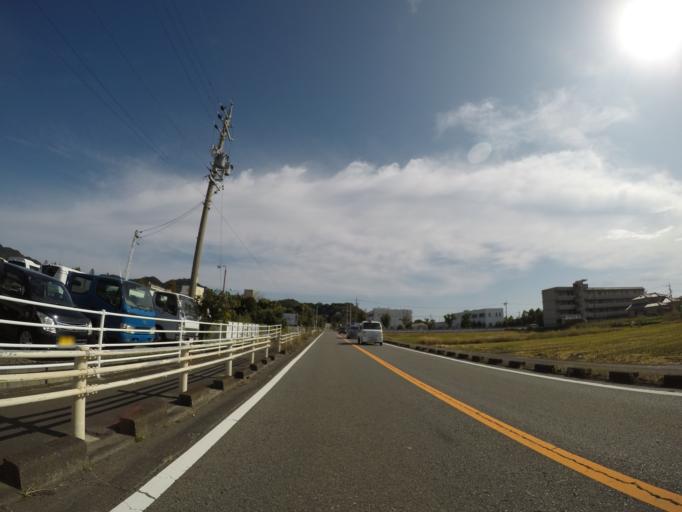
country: JP
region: Shizuoka
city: Yaizu
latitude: 34.8823
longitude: 138.3214
